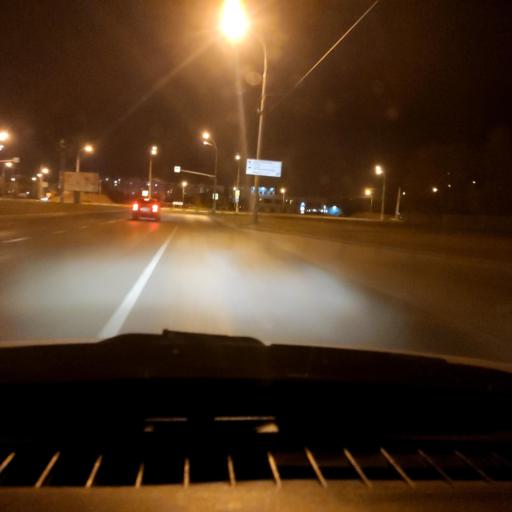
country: RU
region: Samara
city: Tol'yatti
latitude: 53.5251
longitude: 49.3236
